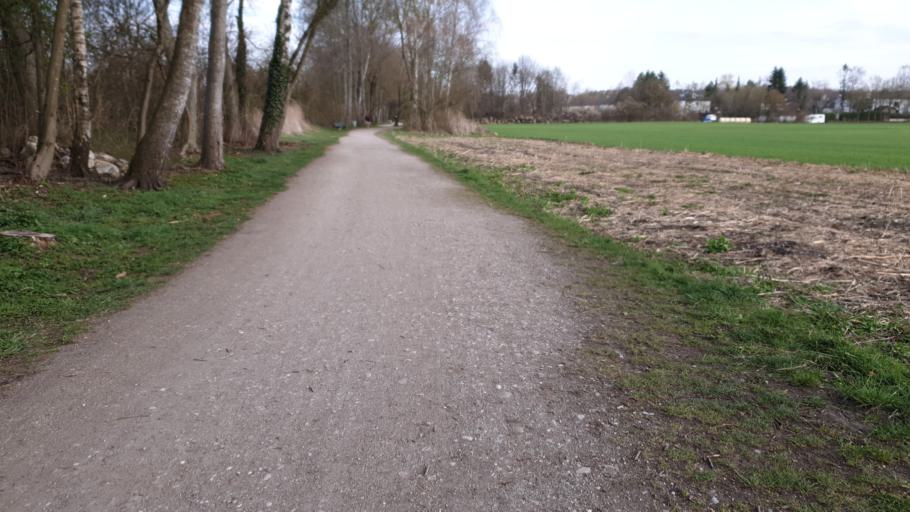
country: DE
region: Bavaria
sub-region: Upper Bavaria
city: Grobenzell
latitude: 48.1772
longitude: 11.3857
